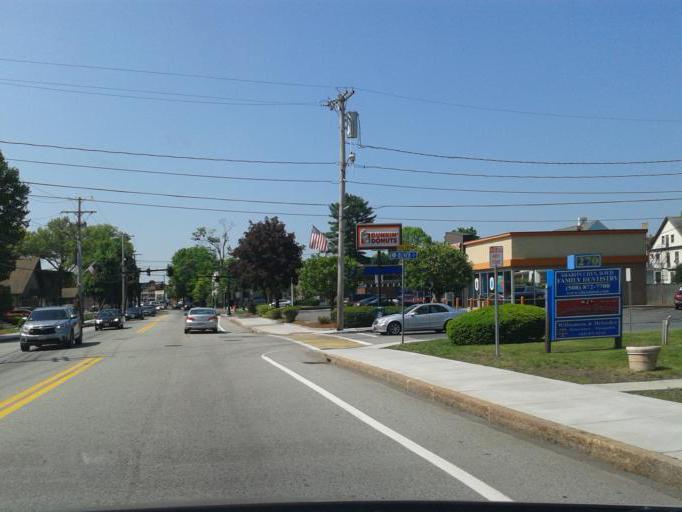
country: US
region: Massachusetts
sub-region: Middlesex County
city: Framingham
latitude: 42.2828
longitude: -71.4147
